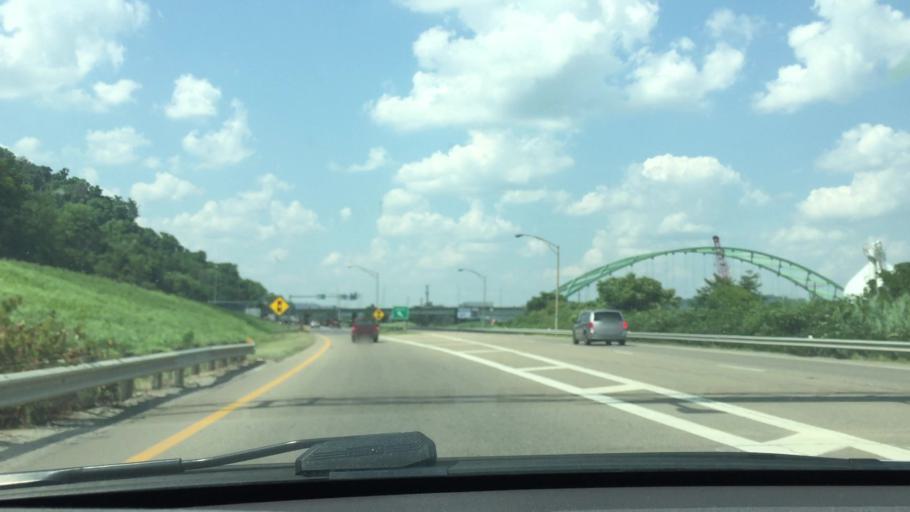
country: US
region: West Virginia
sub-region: Ohio County
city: Wheeling
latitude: 40.0450
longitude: -80.7335
